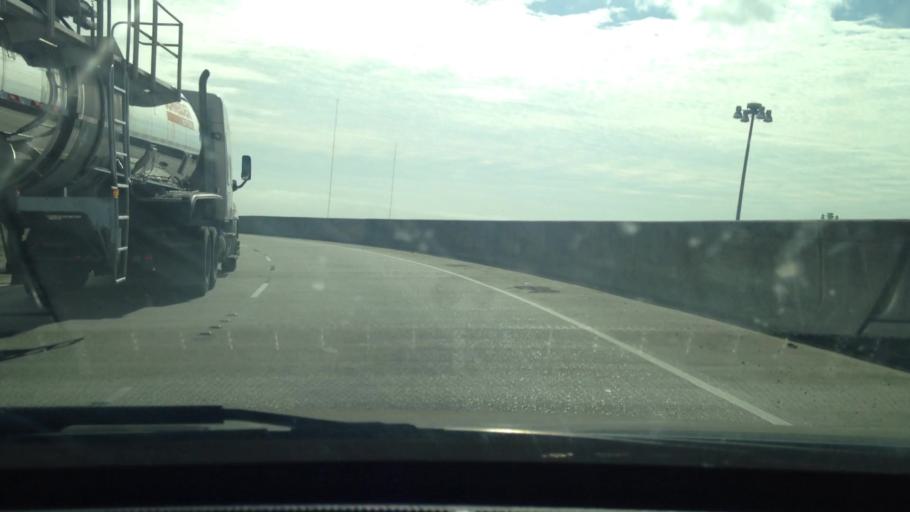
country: US
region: Louisiana
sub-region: Jefferson Parish
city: Terrytown
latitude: 29.9306
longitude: -90.0389
